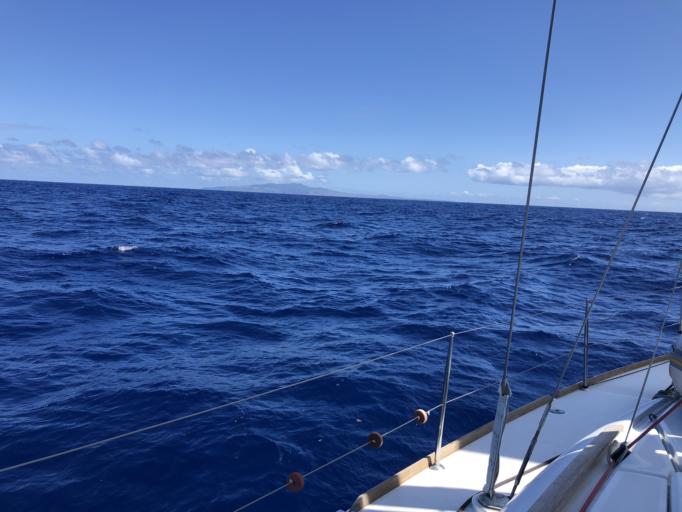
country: PT
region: Azores
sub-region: Vila Franca do Campo
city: Vila Franca do Campo
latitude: 37.1251
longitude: -25.3471
